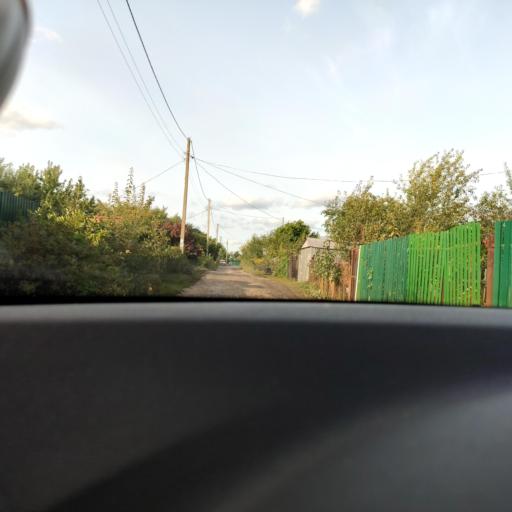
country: RU
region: Samara
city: Petra-Dubrava
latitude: 53.2855
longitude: 50.2947
